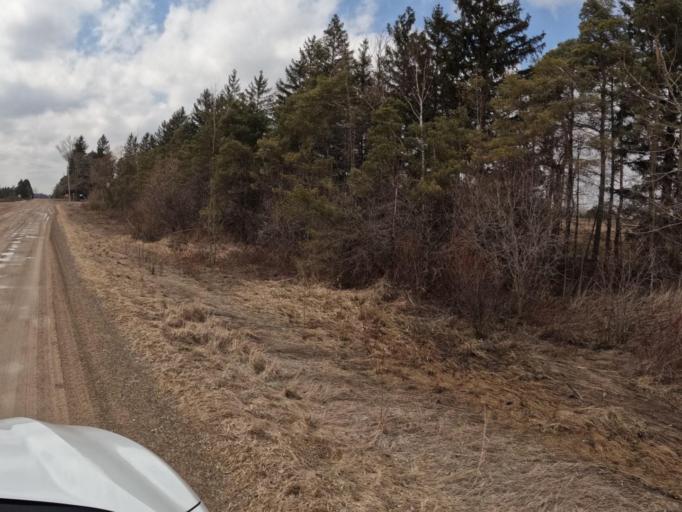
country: CA
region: Ontario
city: Shelburne
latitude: 44.0279
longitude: -80.2615
